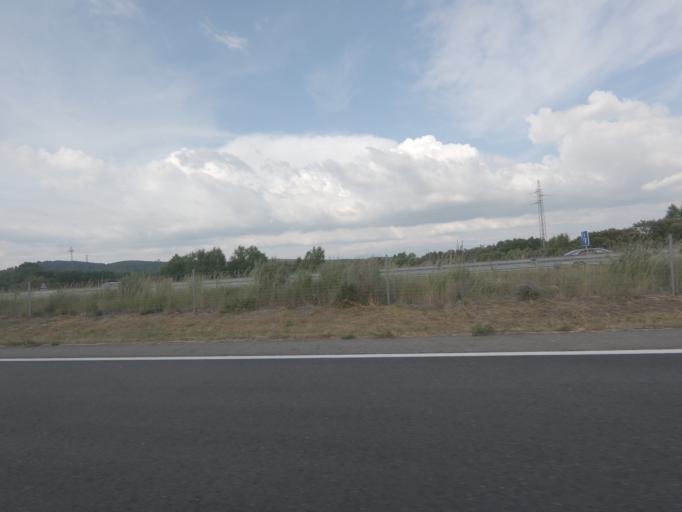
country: ES
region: Galicia
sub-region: Provincia de Ourense
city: Ambia
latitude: 42.1610
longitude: -7.7605
